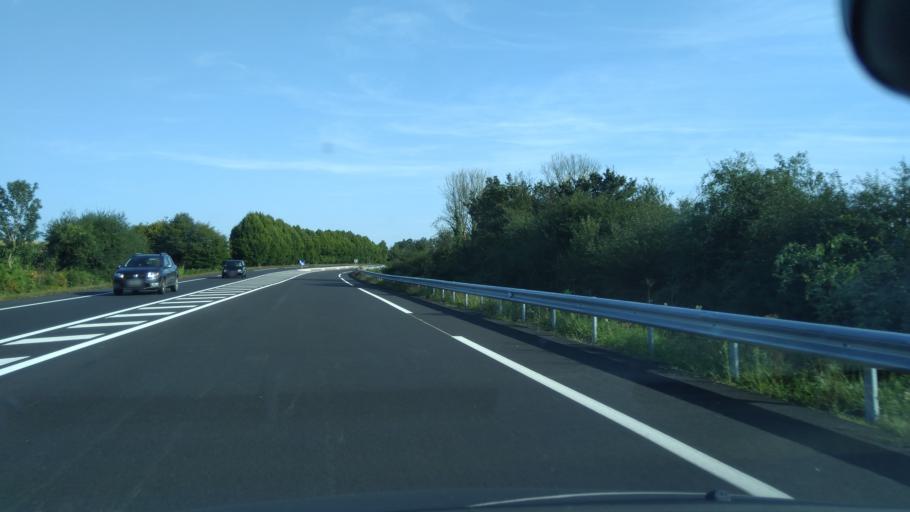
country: FR
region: Pays de la Loire
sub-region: Departement de la Mayenne
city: Entrammes
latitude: 47.9644
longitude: -0.7060
